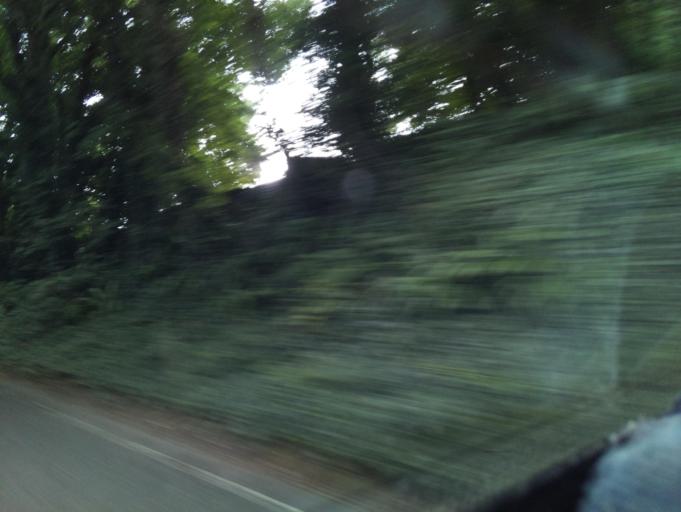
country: GB
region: England
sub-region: North Somerset
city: Nailsea
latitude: 51.4493
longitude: -2.7319
